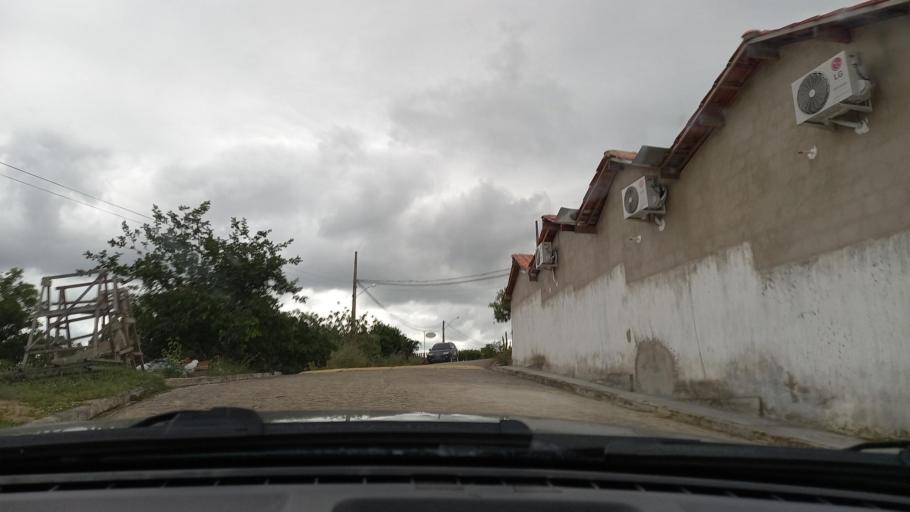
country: BR
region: Sergipe
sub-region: Caninde De Sao Francisco
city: Caninde de Sao Francisco
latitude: -9.6230
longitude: -37.7543
